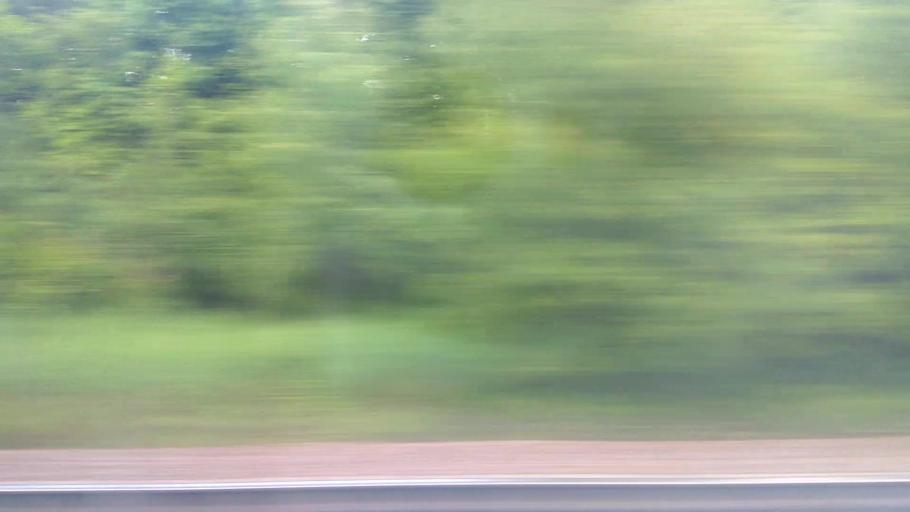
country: RU
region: Moskovskaya
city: Zhilevo
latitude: 55.0667
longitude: 37.9854
